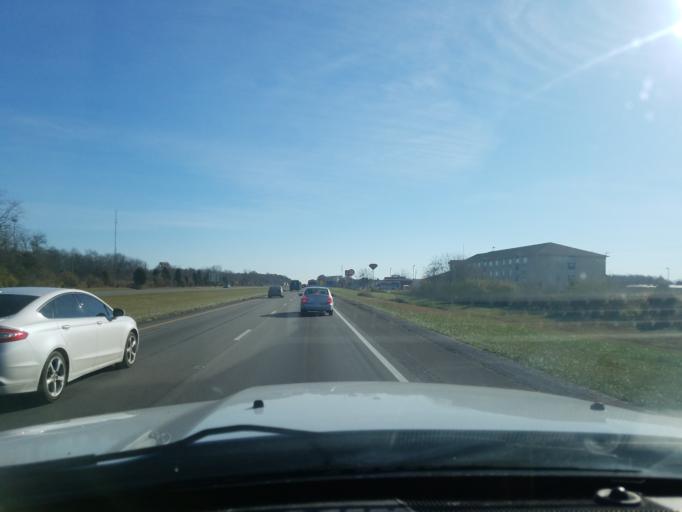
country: US
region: Ohio
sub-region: Clermont County
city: Batavia
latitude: 39.0846
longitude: -84.1560
